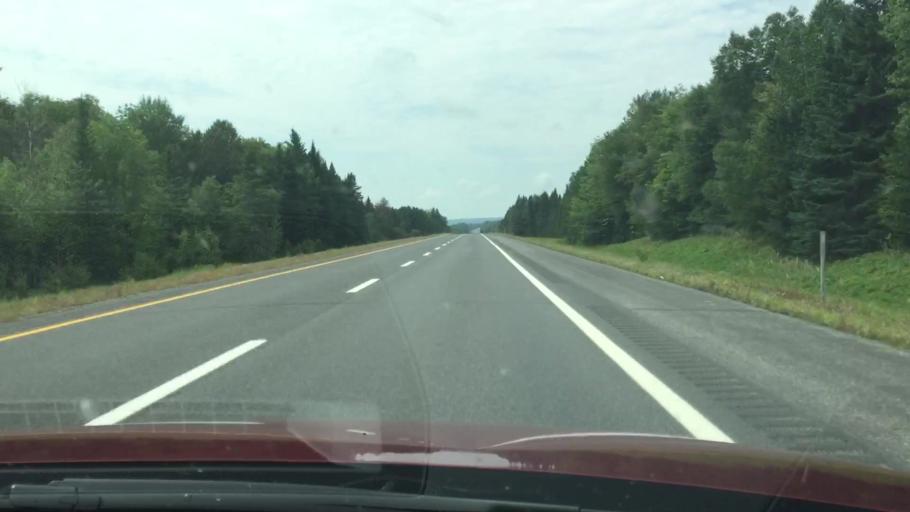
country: US
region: Maine
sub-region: Aroostook County
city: Houlton
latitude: 46.1413
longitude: -67.9689
